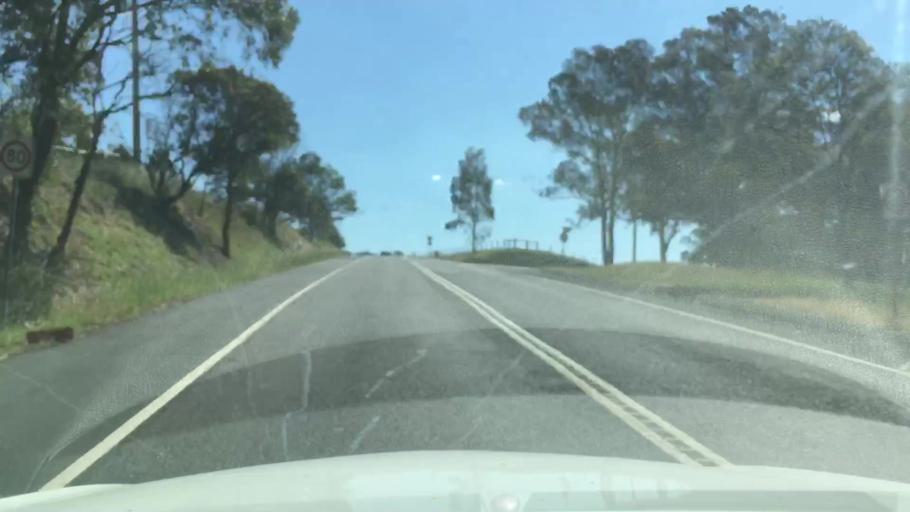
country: AU
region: Victoria
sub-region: Nillumbik
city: North Warrandyte
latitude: -37.6827
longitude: 145.2387
